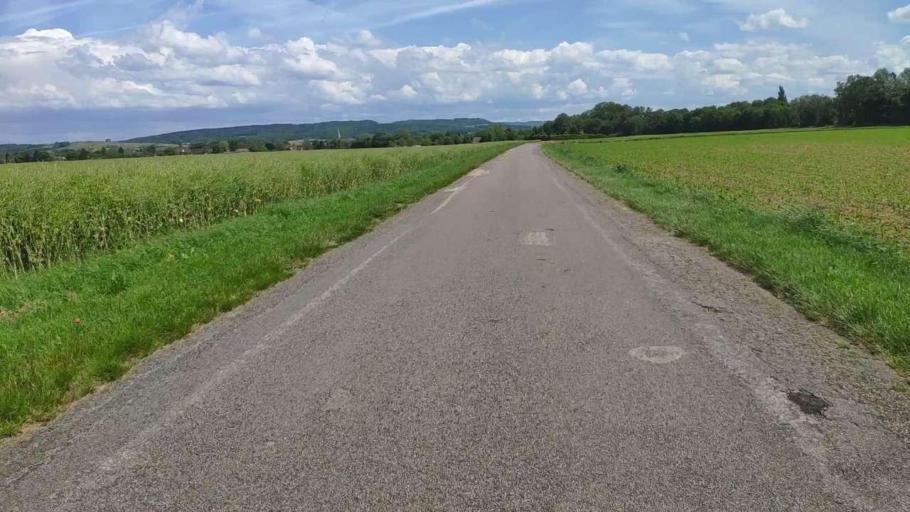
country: FR
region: Franche-Comte
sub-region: Departement du Jura
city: Bletterans
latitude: 46.7493
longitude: 5.4786
